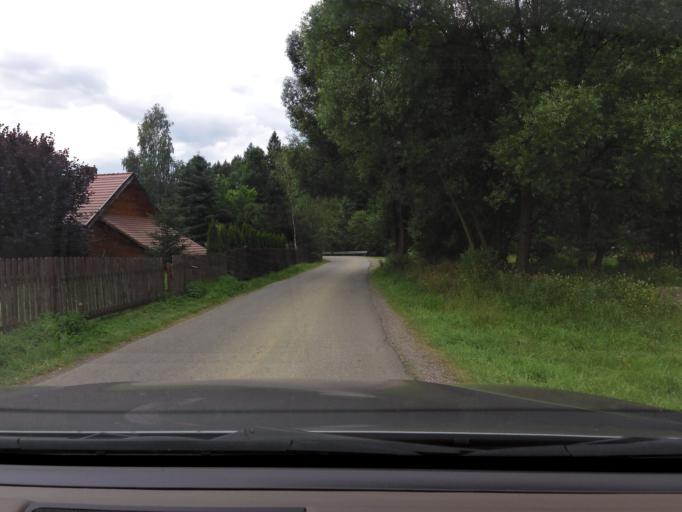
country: PL
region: Silesian Voivodeship
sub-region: Powiat zywiecki
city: Rajcza
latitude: 49.5040
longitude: 19.1164
